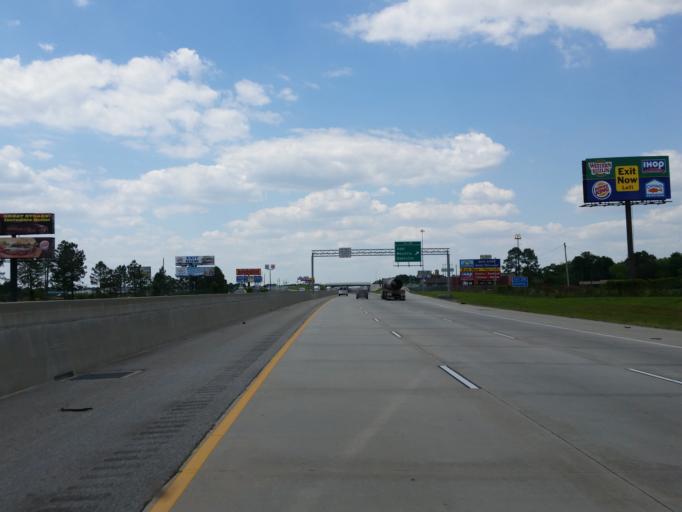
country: US
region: Georgia
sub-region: Cook County
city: Adel
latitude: 31.1293
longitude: -83.4363
